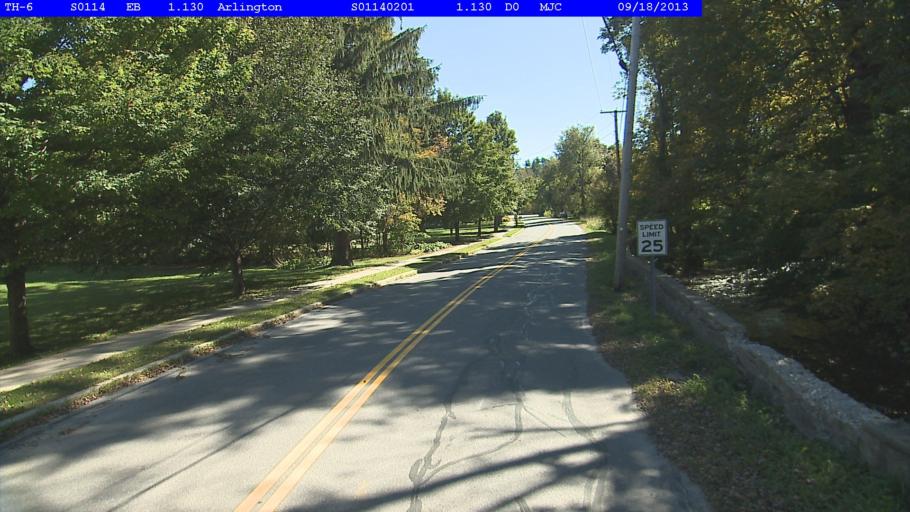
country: US
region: Vermont
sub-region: Bennington County
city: Arlington
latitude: 43.0623
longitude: -73.1431
